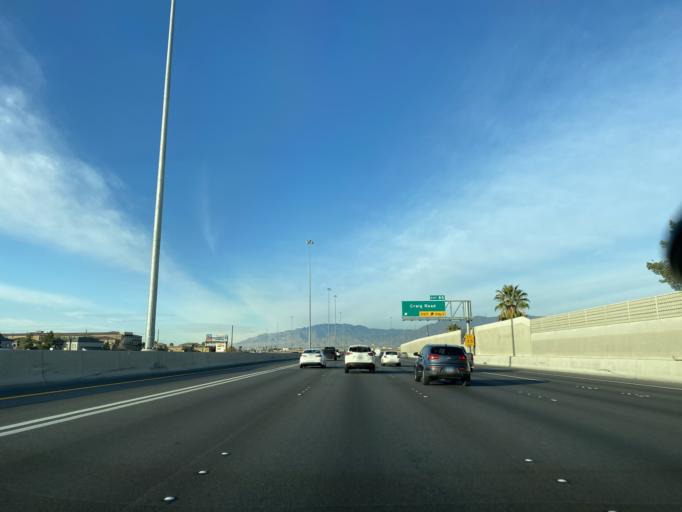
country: US
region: Nevada
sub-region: Clark County
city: Las Vegas
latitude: 36.2341
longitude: -115.2466
